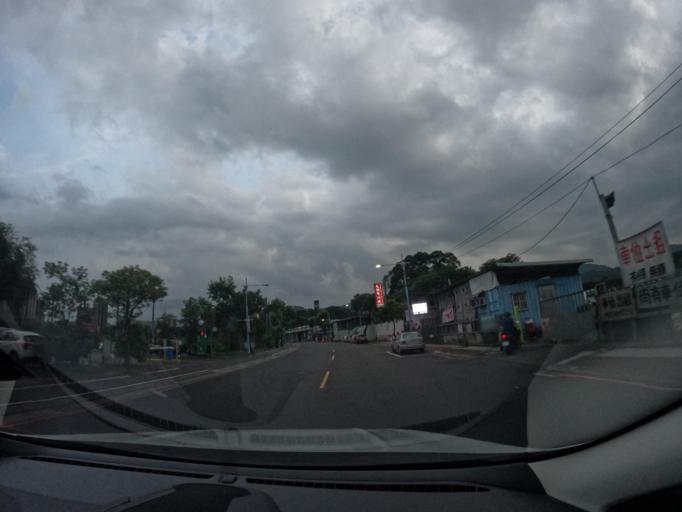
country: TW
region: Taipei
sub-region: Taipei
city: Banqiao
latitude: 24.9790
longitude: 121.4537
